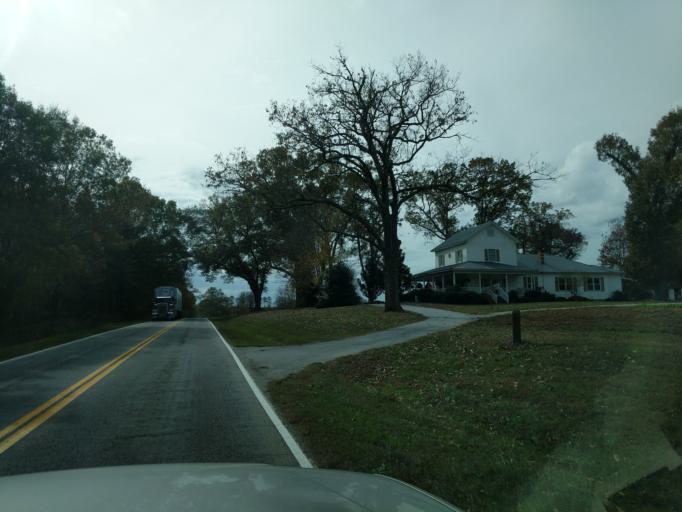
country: US
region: South Carolina
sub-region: Greenwood County
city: Ninety Six
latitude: 34.2378
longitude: -81.8724
